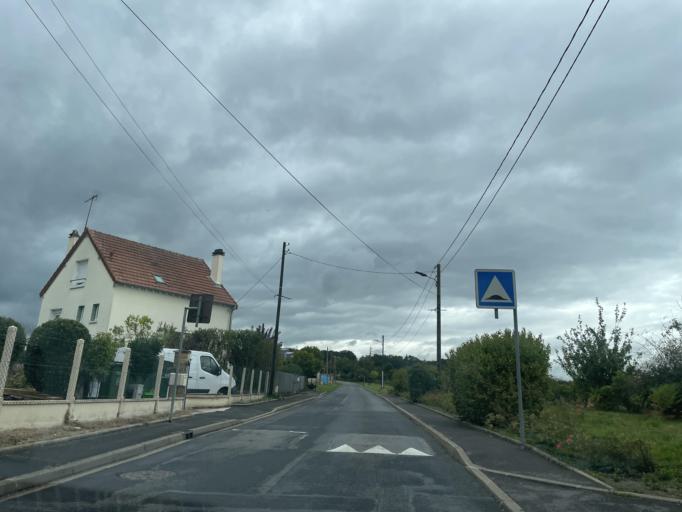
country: FR
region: Ile-de-France
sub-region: Departement de Seine-et-Marne
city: Coulommiers
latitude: 48.8133
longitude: 3.1102
